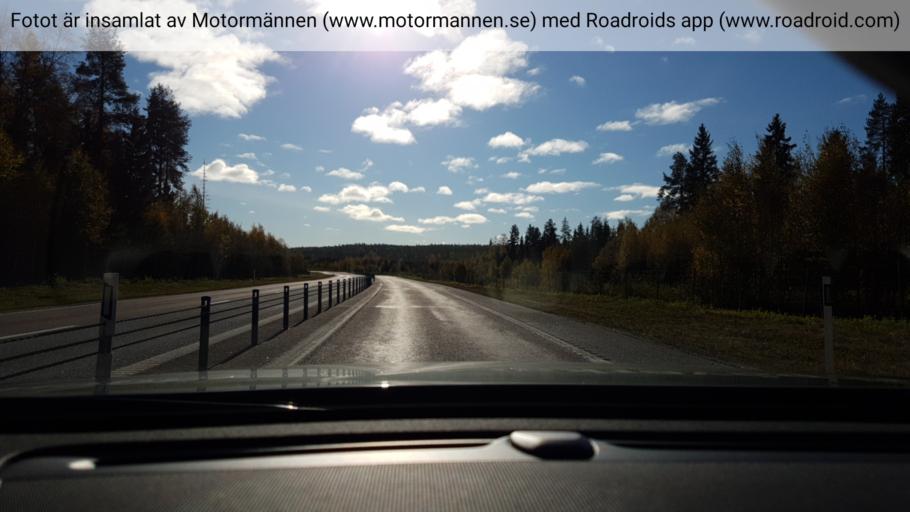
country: SE
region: Vaesterbotten
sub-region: Skelleftea Kommun
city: Skelleftea
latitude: 64.7034
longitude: 21.0007
